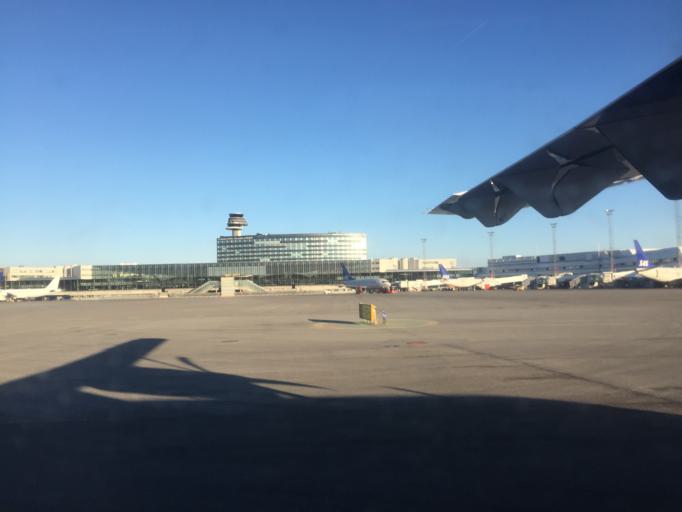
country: SE
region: Stockholm
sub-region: Sigtuna Kommun
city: Marsta
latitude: 59.6495
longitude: 17.9229
